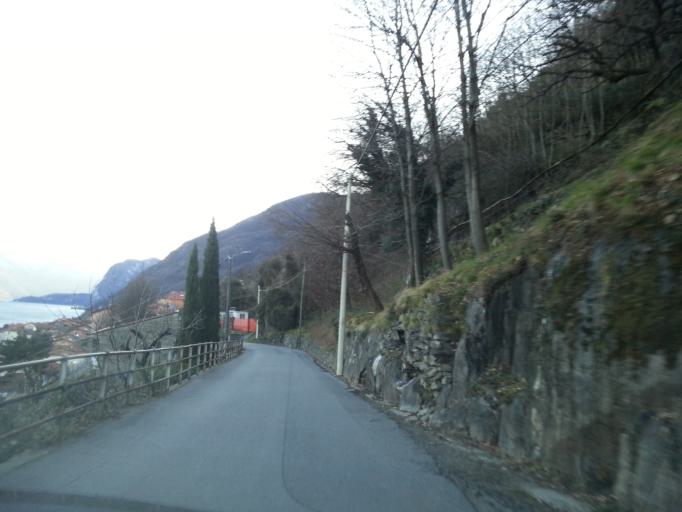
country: IT
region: Lombardy
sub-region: Provincia di Como
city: San Siro
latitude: 46.0663
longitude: 9.2653
